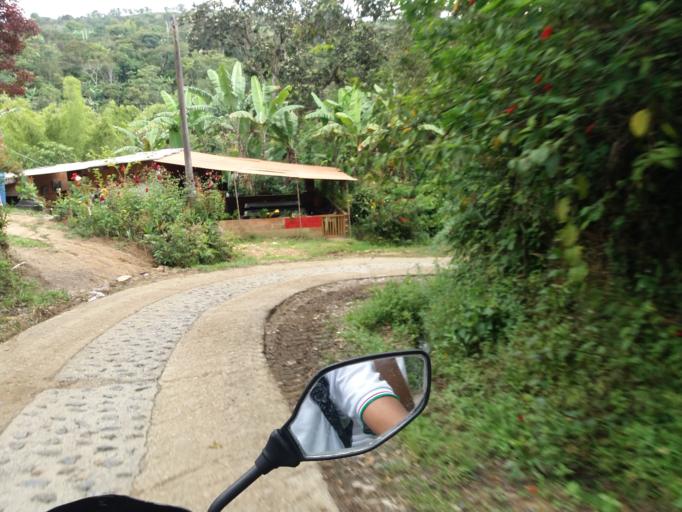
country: CO
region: Santander
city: Guepsa
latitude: 6.0060
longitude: -73.5452
